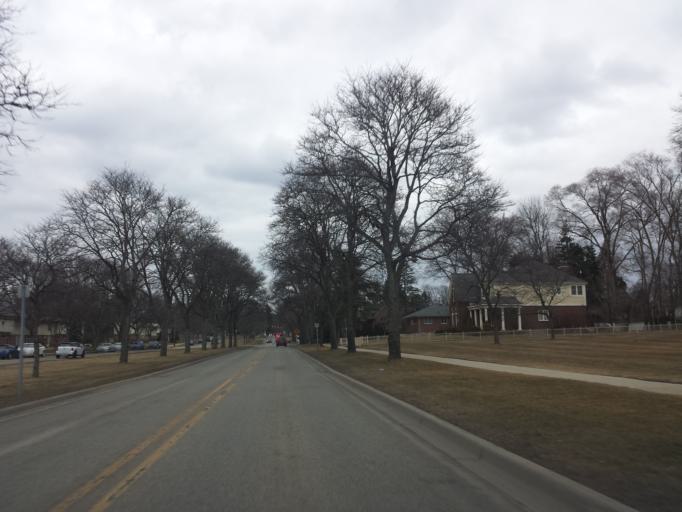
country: US
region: Michigan
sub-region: Oakland County
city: Beverly Hills
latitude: 42.5351
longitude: -83.2241
